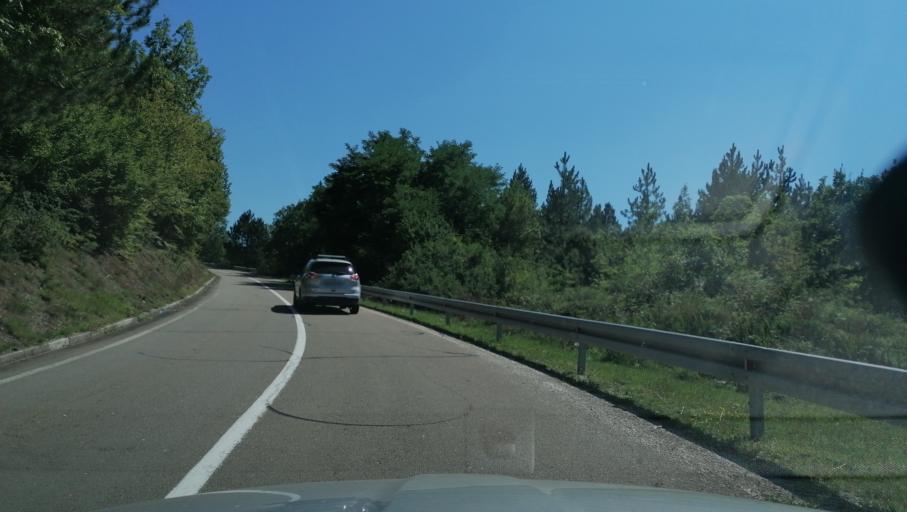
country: RS
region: Central Serbia
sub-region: Raski Okrug
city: Raska
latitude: 43.4637
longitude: 20.5596
